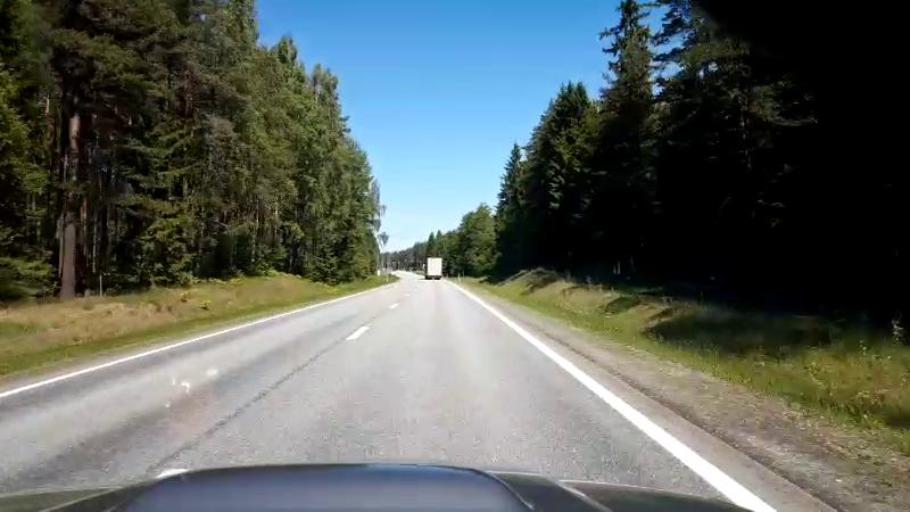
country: LV
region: Salacgrivas
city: Salacgriva
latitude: 57.5696
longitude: 24.4344
